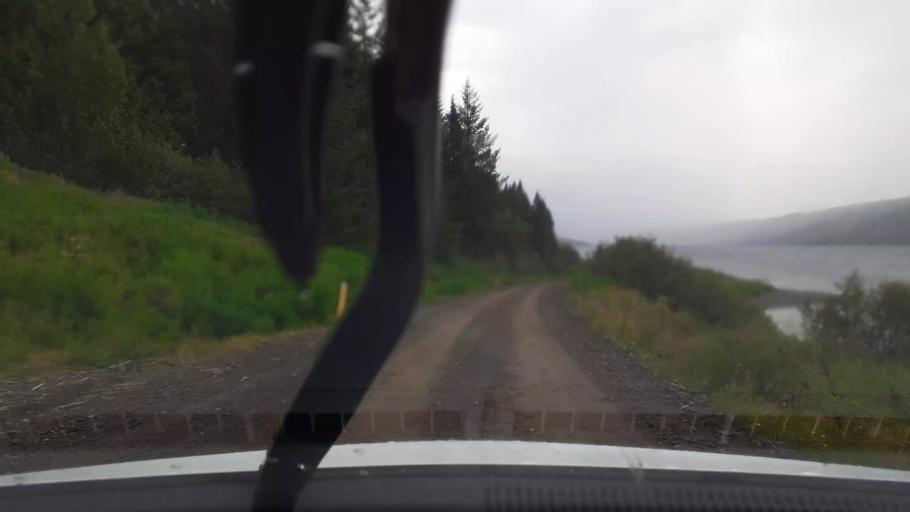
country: IS
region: Capital Region
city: Mosfellsbaer
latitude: 64.5151
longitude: -21.4127
